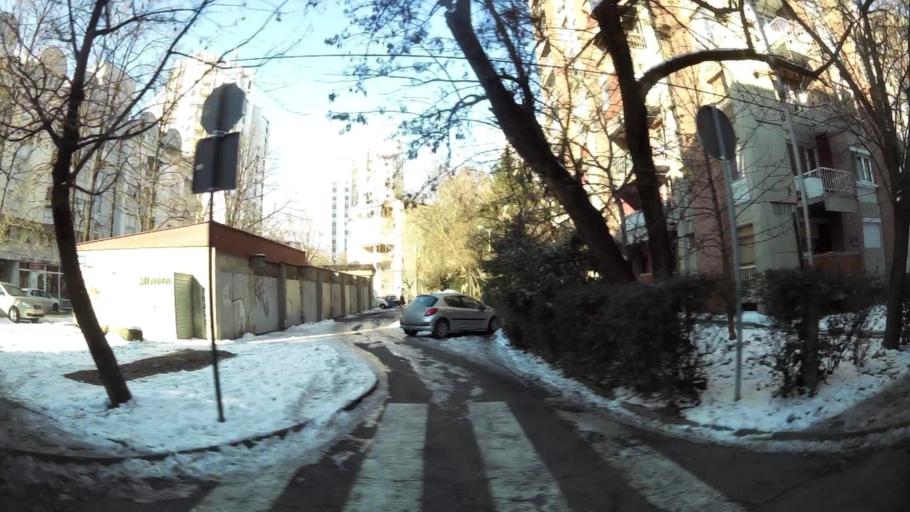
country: MK
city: Krushopek
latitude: 42.0077
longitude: 21.3854
